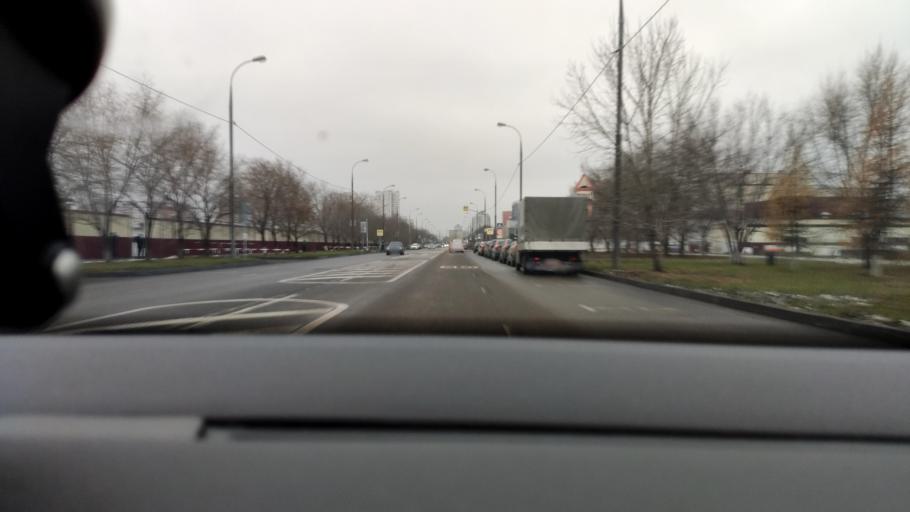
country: RU
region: Moscow
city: Kuz'minki
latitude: 55.6739
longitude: 37.7874
